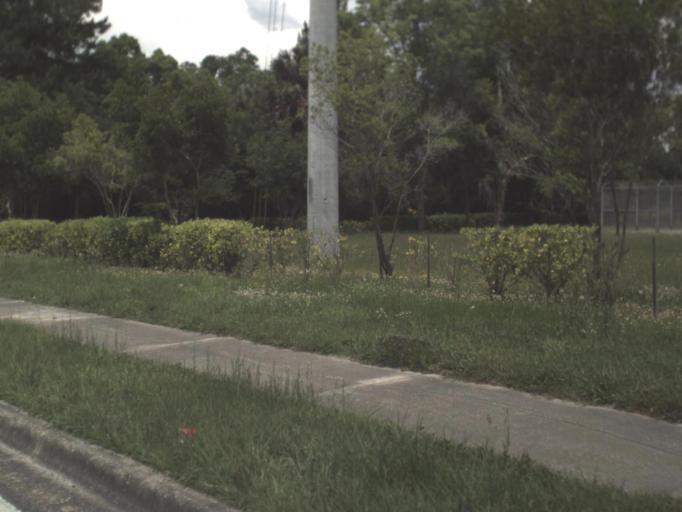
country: US
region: Florida
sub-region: Columbia County
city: Five Points
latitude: 30.2205
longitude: -82.6382
